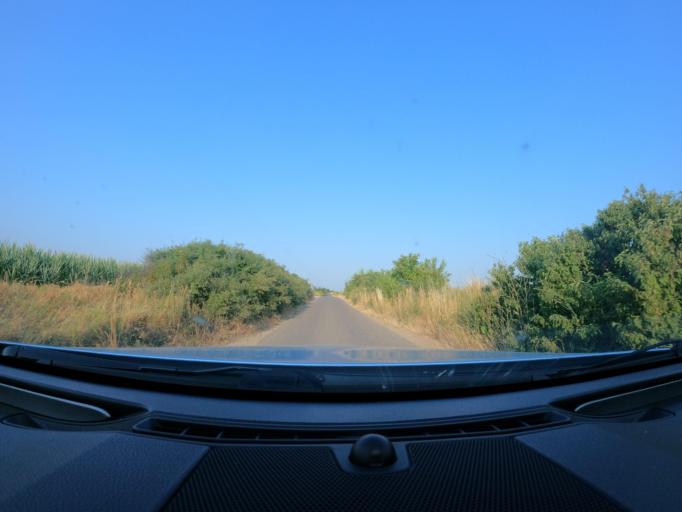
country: RS
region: Autonomna Pokrajina Vojvodina
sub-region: Sremski Okrug
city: Ruma
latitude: 45.0521
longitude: 19.7713
